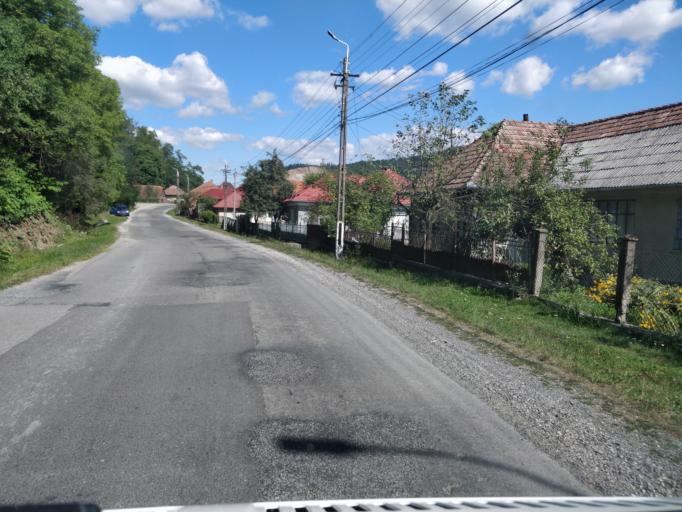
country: RO
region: Cluj
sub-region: Comuna Poeni
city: Poeni
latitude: 46.8844
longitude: 22.8783
